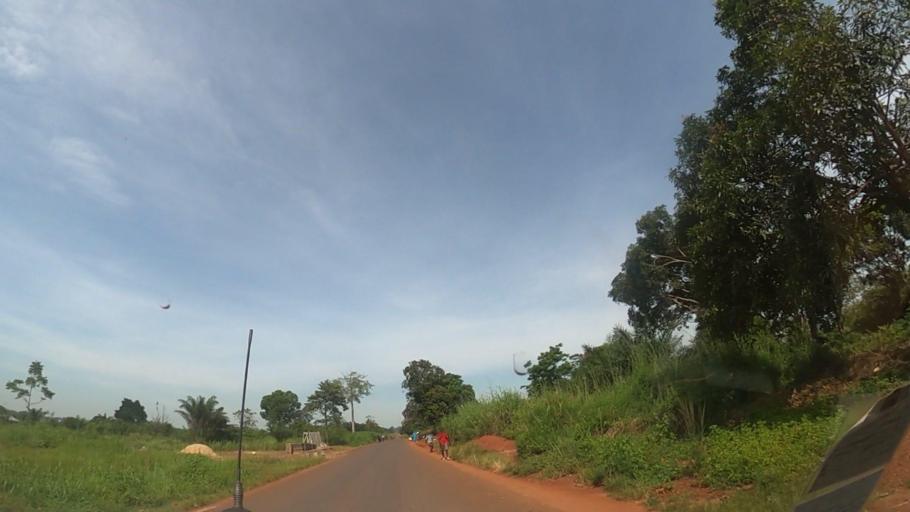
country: CF
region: Ombella-Mpoko
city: Bimbo
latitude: 4.3141
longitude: 18.4709
